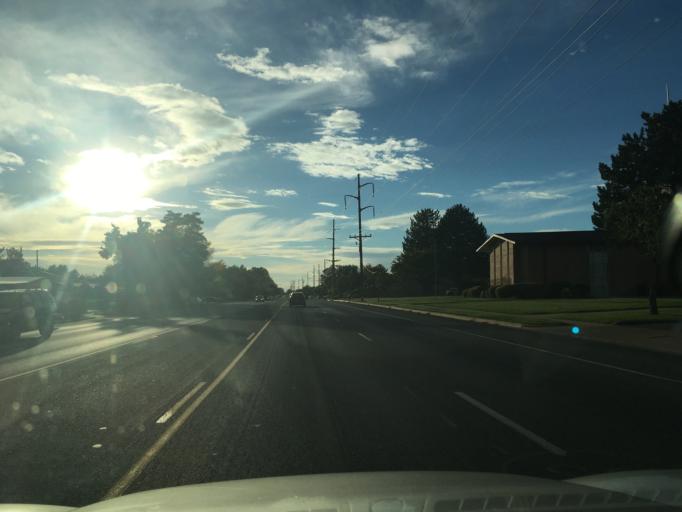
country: US
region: Utah
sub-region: Davis County
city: Layton
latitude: 41.0747
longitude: -111.9654
